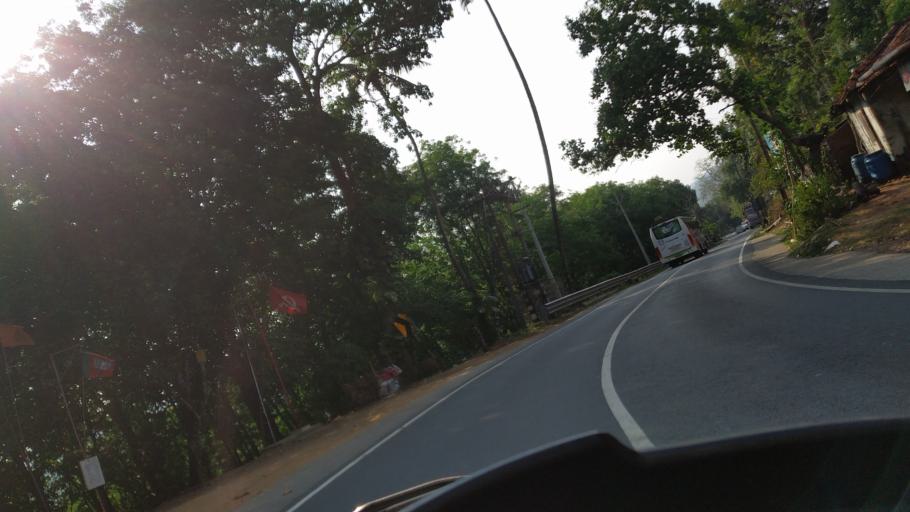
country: IN
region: Kerala
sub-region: Kottayam
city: Erattupetta
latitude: 9.5344
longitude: 76.9144
